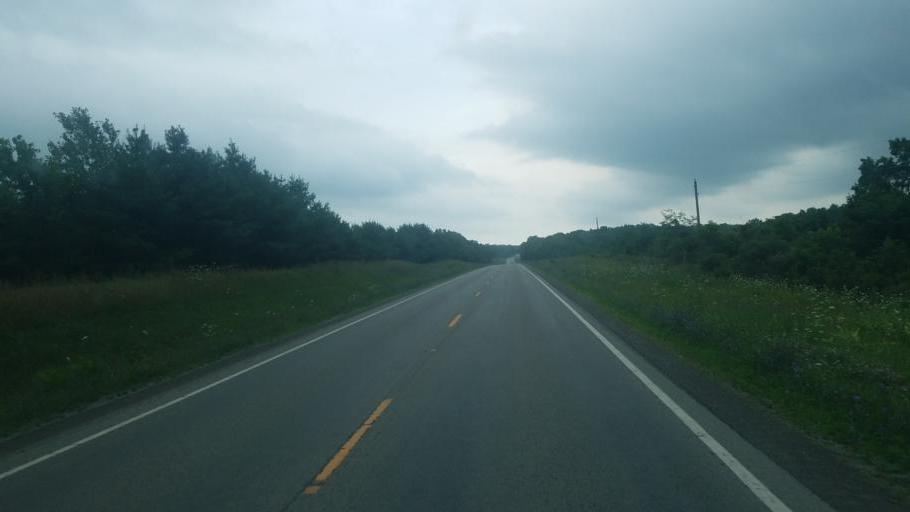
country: US
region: Ohio
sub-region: Logan County
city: Russells Point
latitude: 40.5733
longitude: -83.8381
